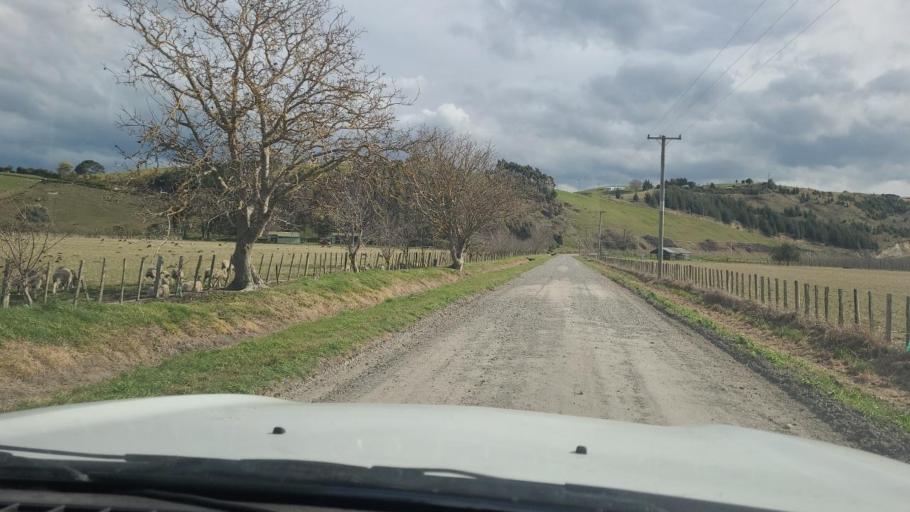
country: NZ
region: Hawke's Bay
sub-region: Napier City
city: Taradale
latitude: -39.5635
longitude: 176.7641
